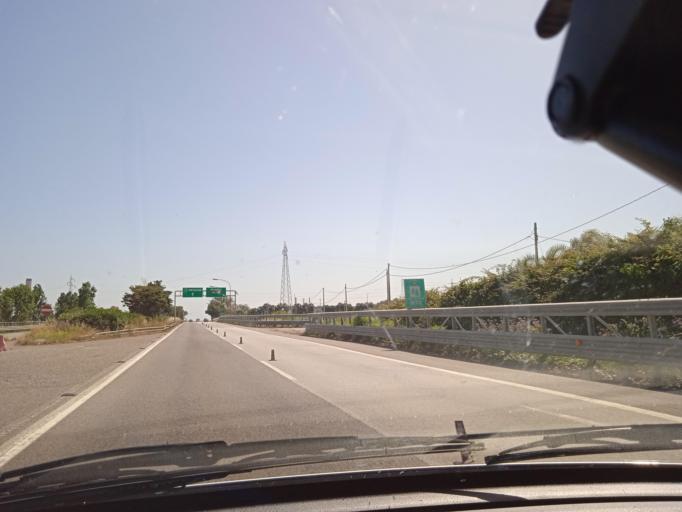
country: IT
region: Sicily
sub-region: Messina
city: San Filippo del Mela
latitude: 38.1895
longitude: 15.2689
